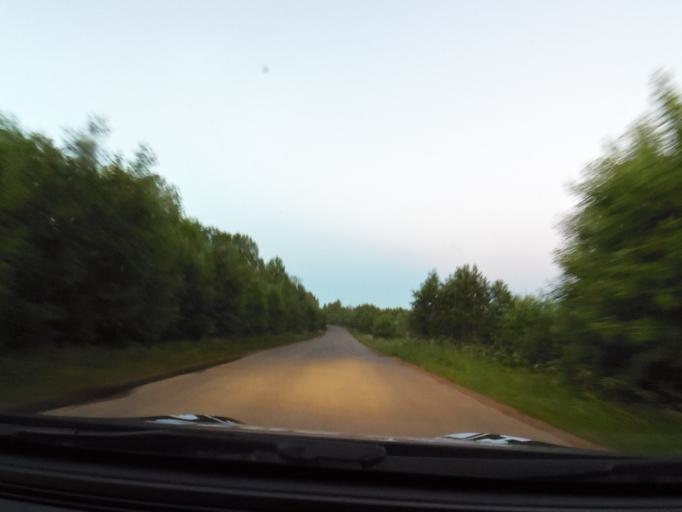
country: RU
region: Vologda
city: Vytegra
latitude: 60.9977
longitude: 36.3238
